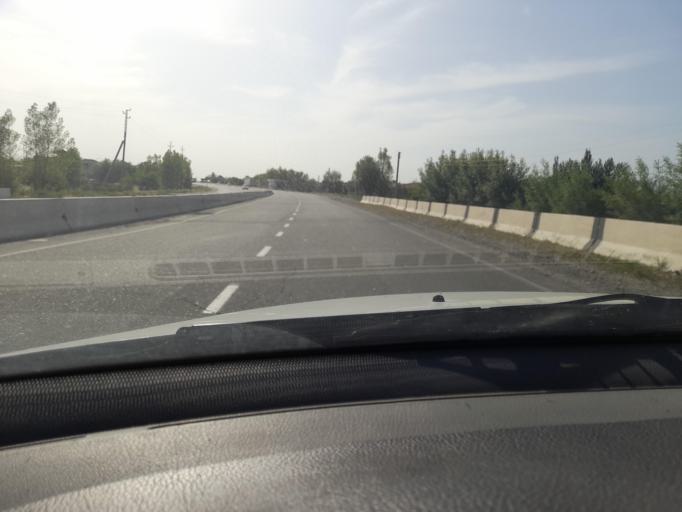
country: UZ
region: Samarqand
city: Kattaqo'rg'on
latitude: 39.9288
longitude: 66.2692
